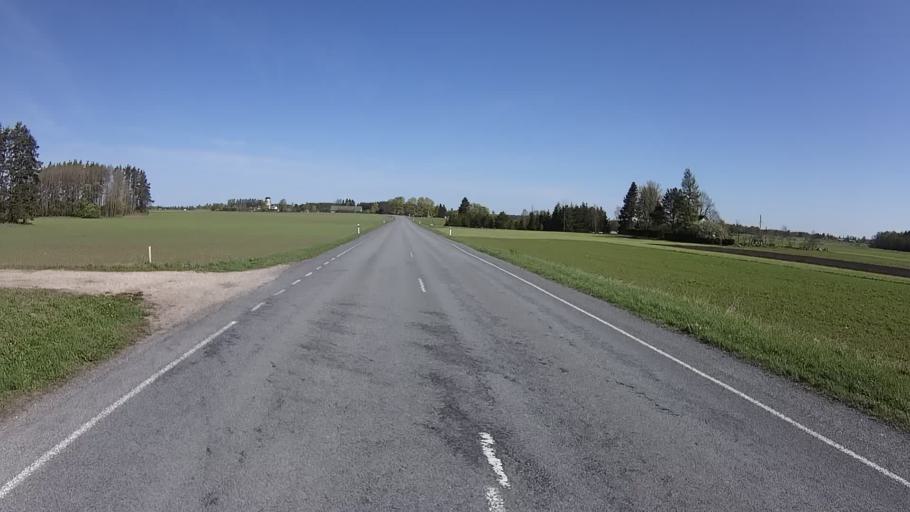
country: EE
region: Raplamaa
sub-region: Kehtna vald
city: Kehtna
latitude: 58.8950
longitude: 24.7883
